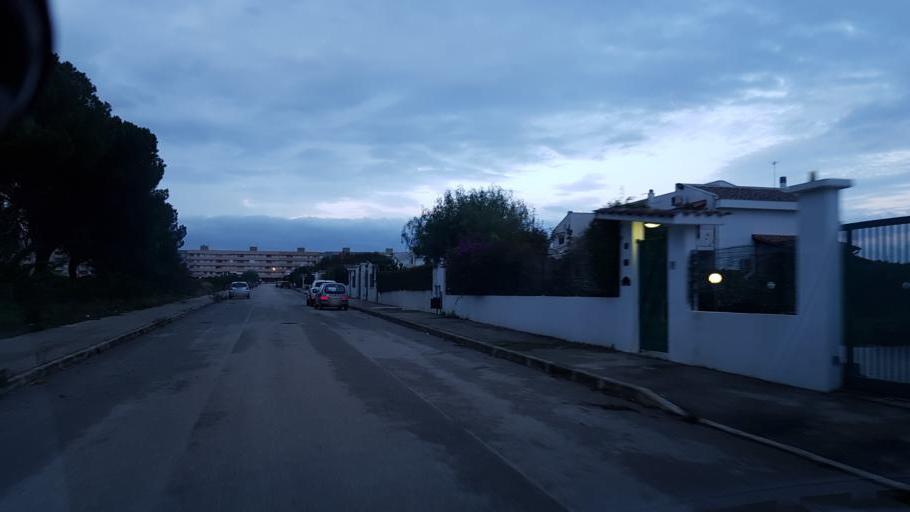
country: IT
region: Apulia
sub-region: Provincia di Taranto
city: Paolo VI
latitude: 40.5280
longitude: 17.2847
